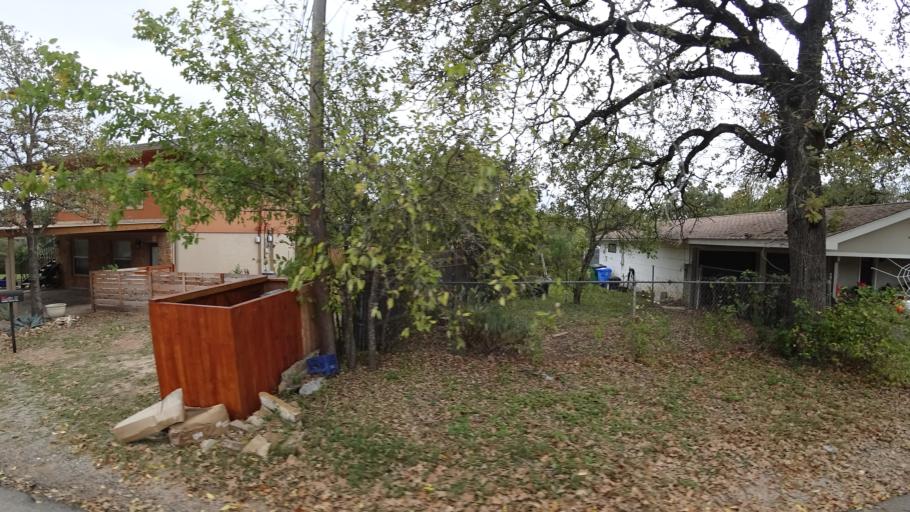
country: US
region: Texas
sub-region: Travis County
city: Bee Cave
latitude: 30.3328
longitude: -97.9249
